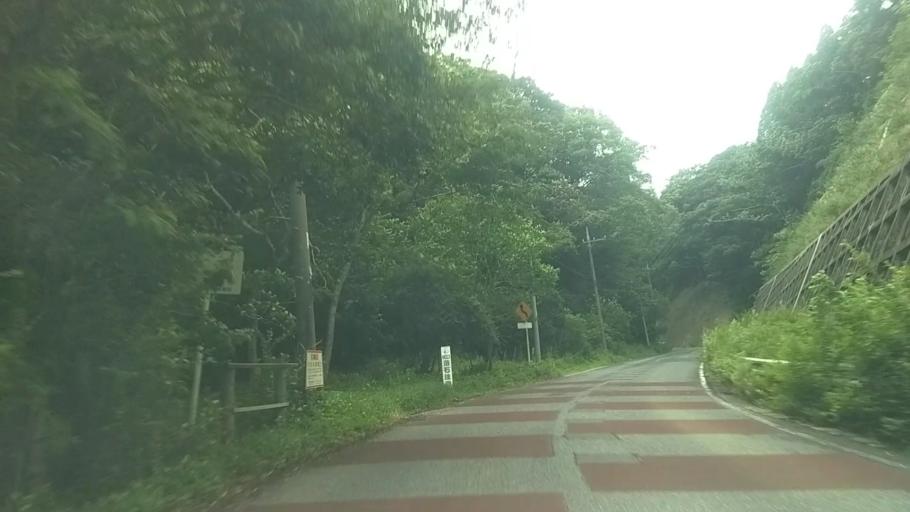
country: JP
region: Chiba
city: Kawaguchi
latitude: 35.2287
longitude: 140.0294
